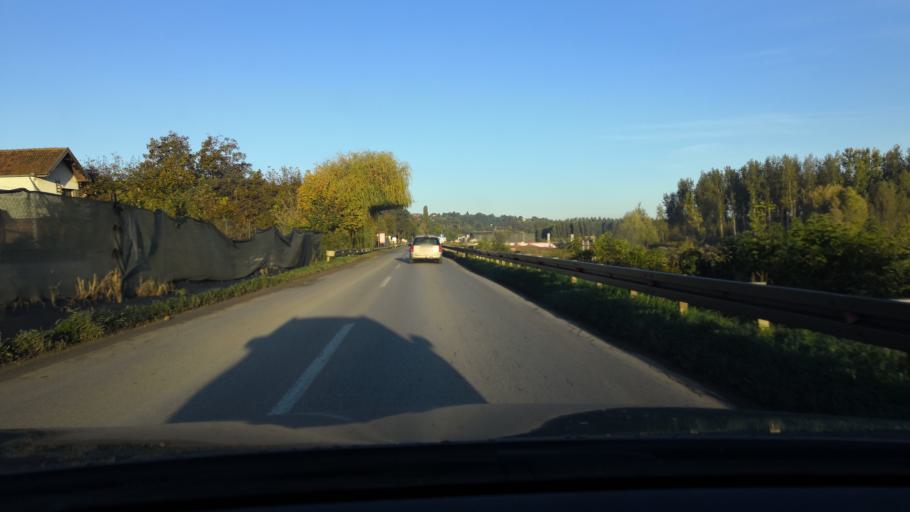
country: RS
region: Autonomna Pokrajina Vojvodina
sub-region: Juznobacki Okrug
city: Sremski Karlovci
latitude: 45.2097
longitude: 19.9235
